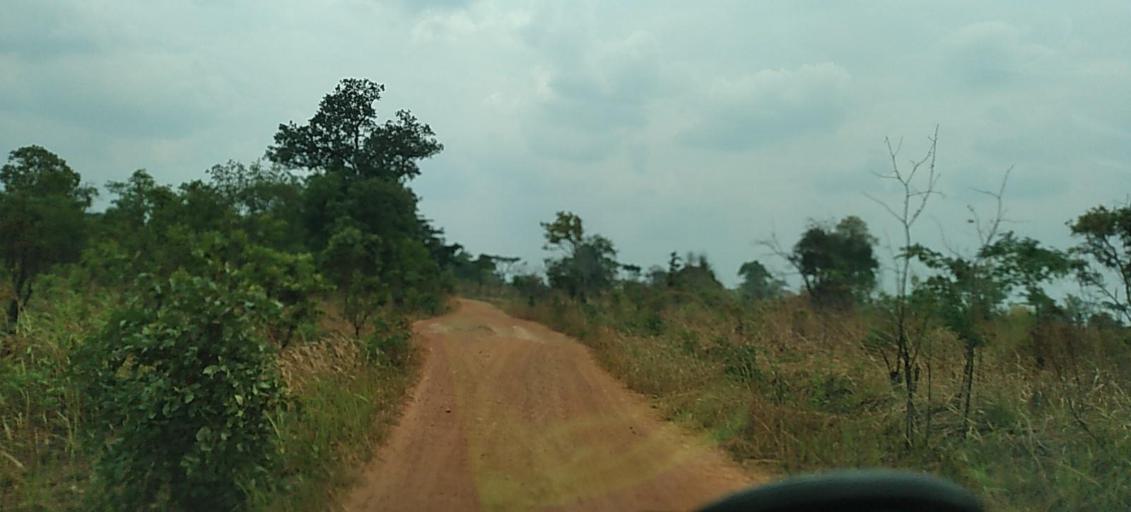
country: ZM
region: North-Western
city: Kansanshi
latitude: -12.0780
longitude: 26.3582
